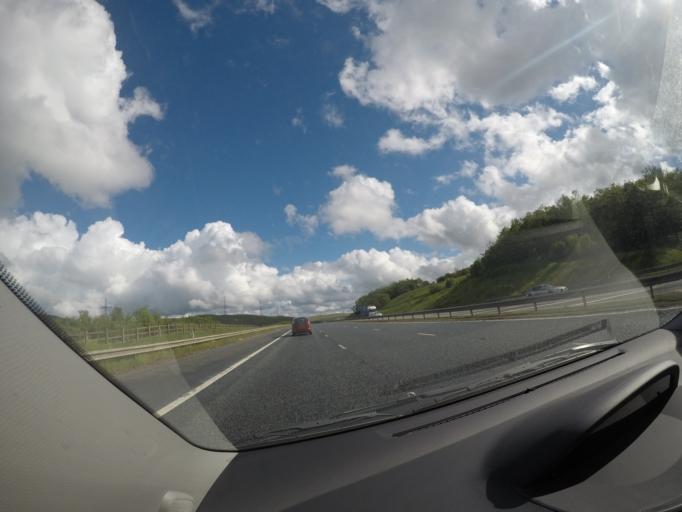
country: GB
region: Scotland
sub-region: South Lanarkshire
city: Douglas
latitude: 55.5588
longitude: -3.8030
